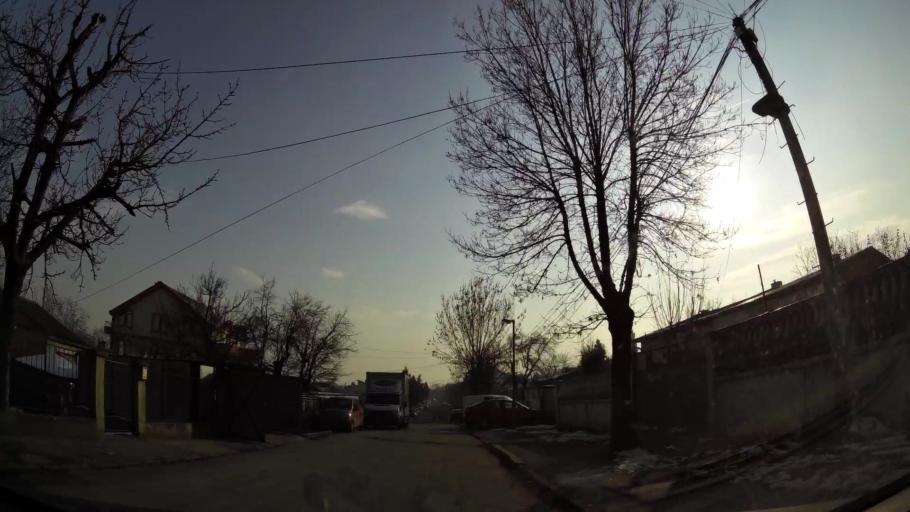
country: MK
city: Creshevo
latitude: 42.0159
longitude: 21.5083
